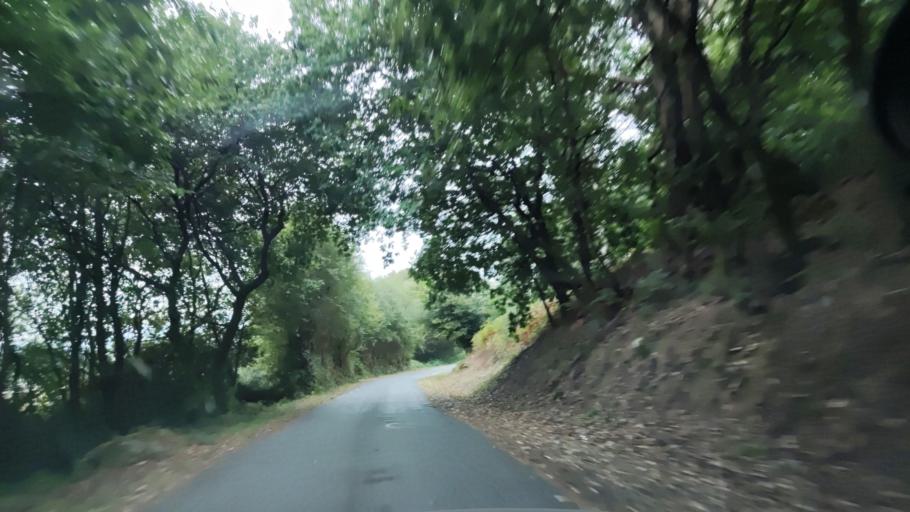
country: ES
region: Galicia
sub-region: Provincia de Pontevedra
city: Catoira
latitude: 42.7075
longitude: -8.7224
